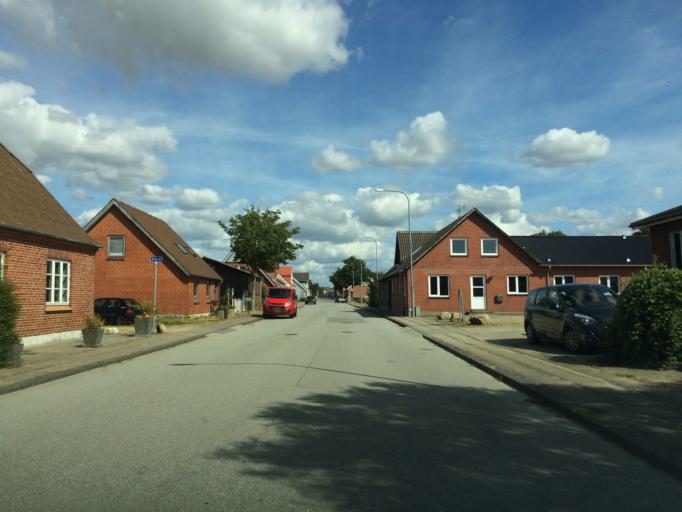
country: DK
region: Central Jutland
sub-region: Ringkobing-Skjern Kommune
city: Skjern
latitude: 56.0258
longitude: 8.3803
